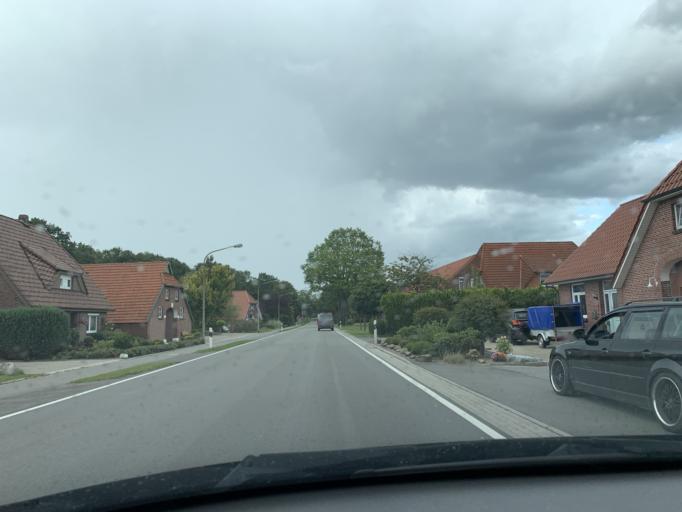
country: DE
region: Lower Saxony
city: Westerstede
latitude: 53.2819
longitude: 7.9795
